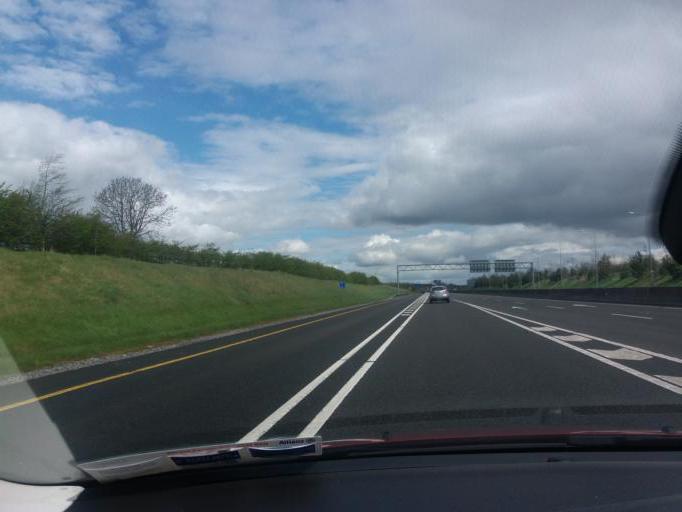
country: IE
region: Leinster
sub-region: Laois
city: Mountrath
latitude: 52.9247
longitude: -7.4776
